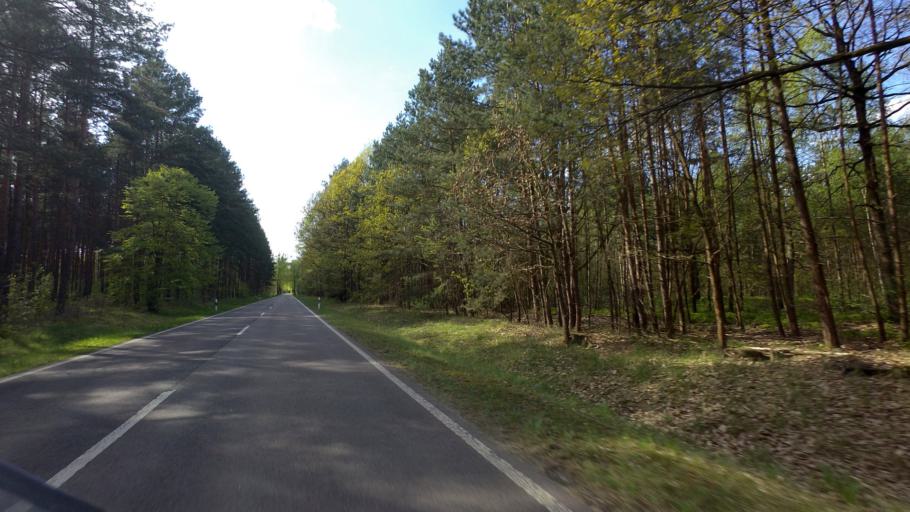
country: DE
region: Brandenburg
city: Friedrichswalde
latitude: 53.0015
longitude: 13.5910
